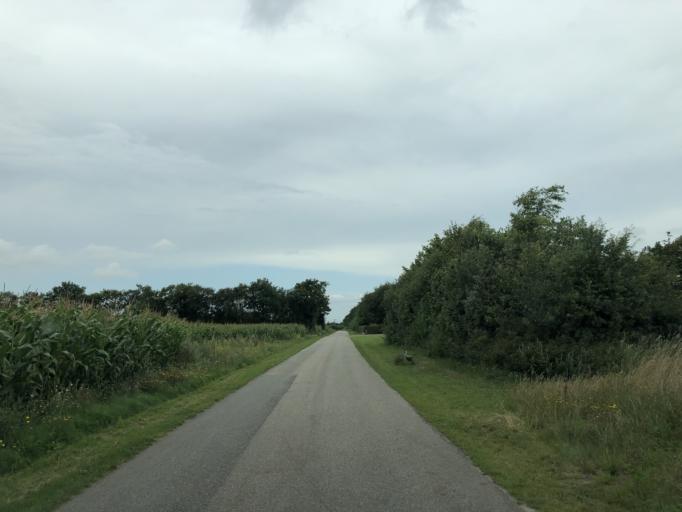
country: DK
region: Central Jutland
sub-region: Ringkobing-Skjern Kommune
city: Ringkobing
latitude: 56.1307
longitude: 8.2601
